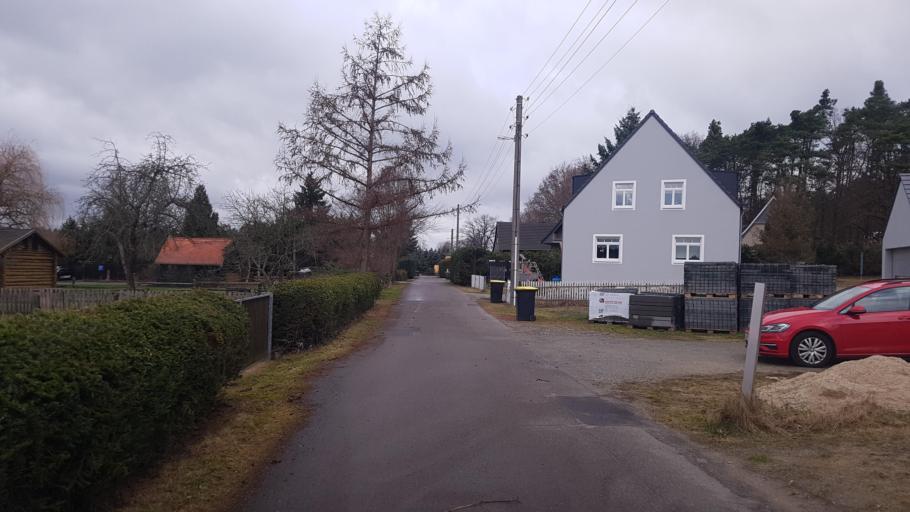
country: DE
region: Brandenburg
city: Kroppen
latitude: 51.3794
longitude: 13.8006
